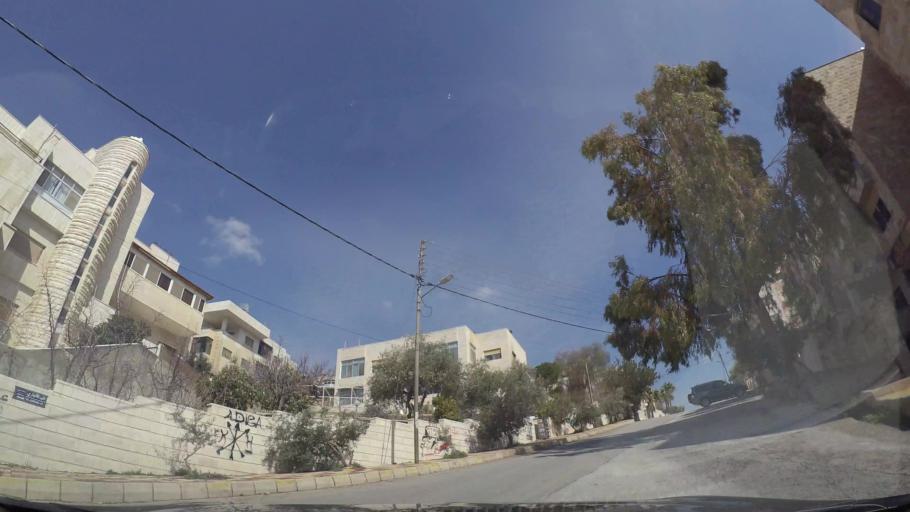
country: JO
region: Amman
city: Al Jubayhah
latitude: 31.9902
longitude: 35.8991
